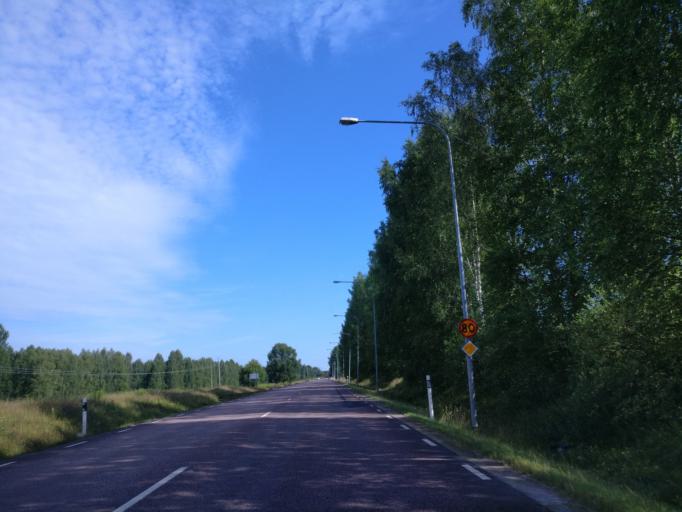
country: SE
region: Vaermland
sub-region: Hagfors Kommun
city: Hagfors
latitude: 60.0497
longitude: 13.7042
